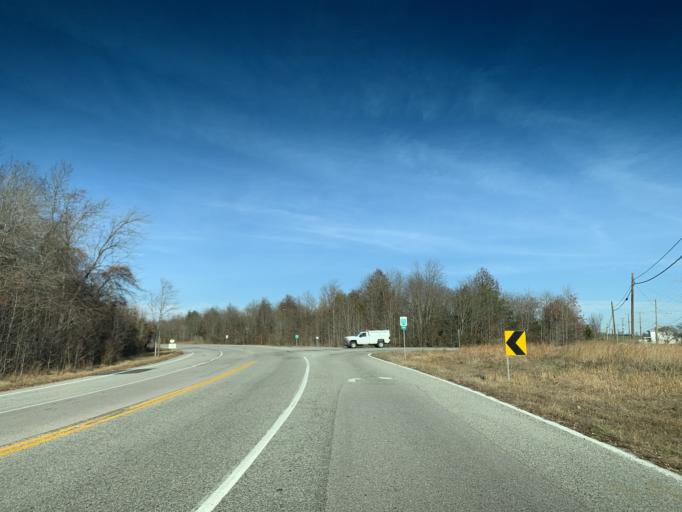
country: US
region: Maryland
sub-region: Cecil County
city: Perryville
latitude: 39.5647
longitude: -76.0617
